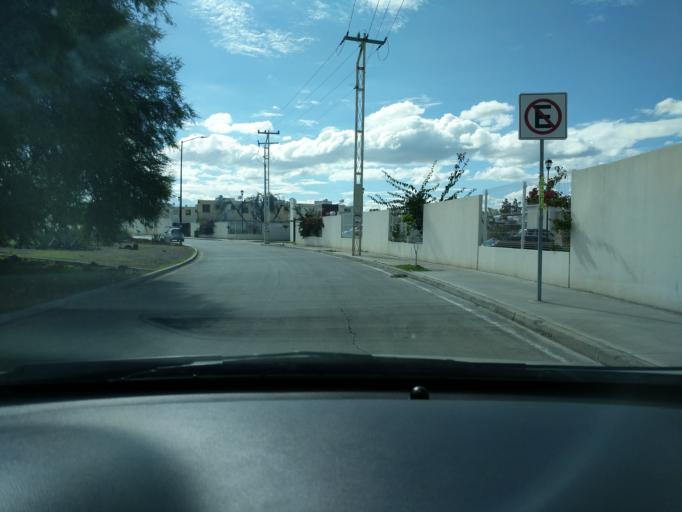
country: MX
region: Queretaro
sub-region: El Marques
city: La Loma
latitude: 20.5850
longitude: -100.2546
